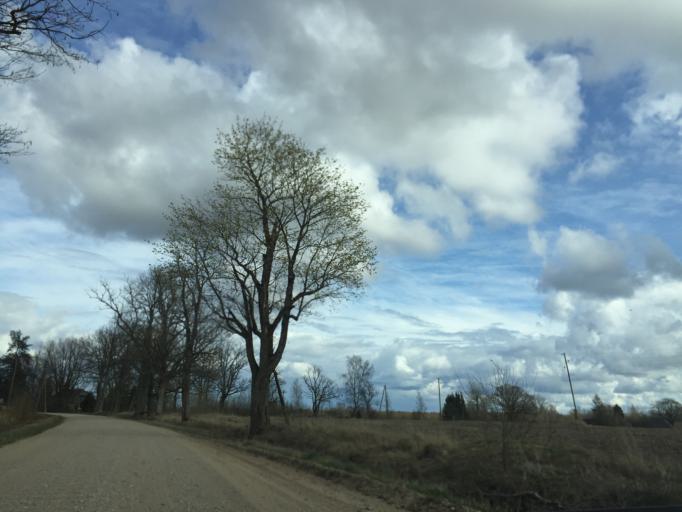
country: LV
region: Limbazu Rajons
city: Limbazi
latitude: 57.6108
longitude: 24.7462
